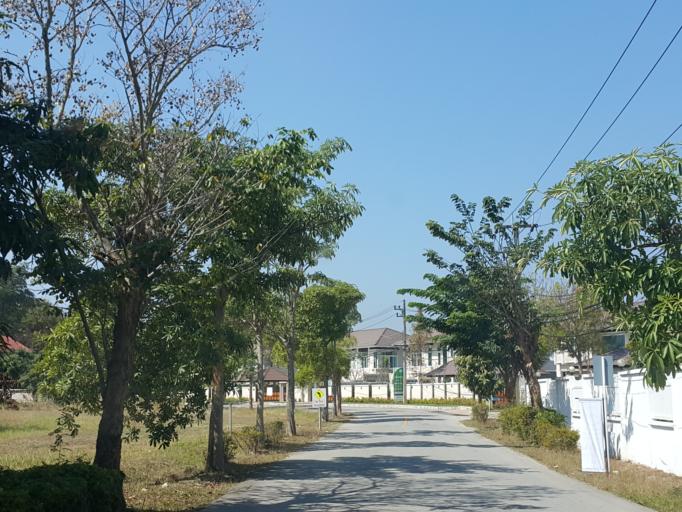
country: TH
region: Chiang Mai
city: Chiang Mai
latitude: 18.7343
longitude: 98.9682
